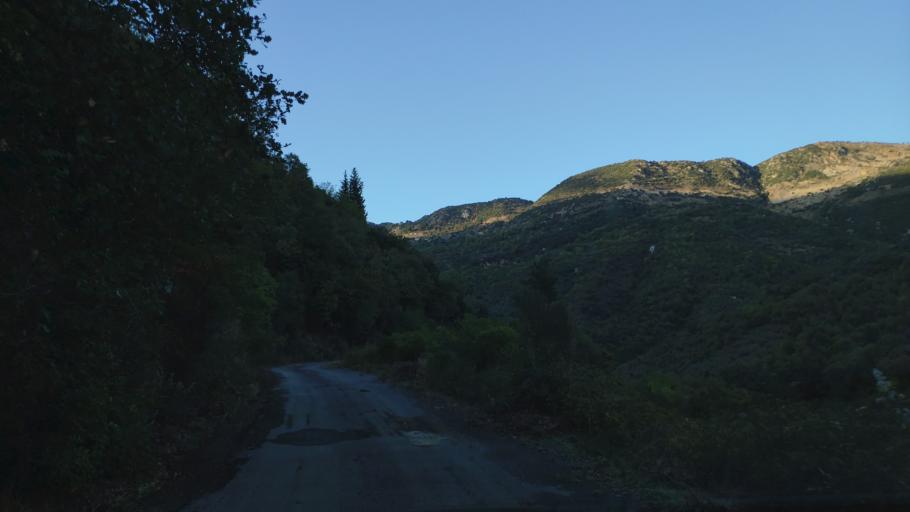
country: GR
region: Peloponnese
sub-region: Nomos Arkadias
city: Dimitsana
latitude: 37.5691
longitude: 22.0420
